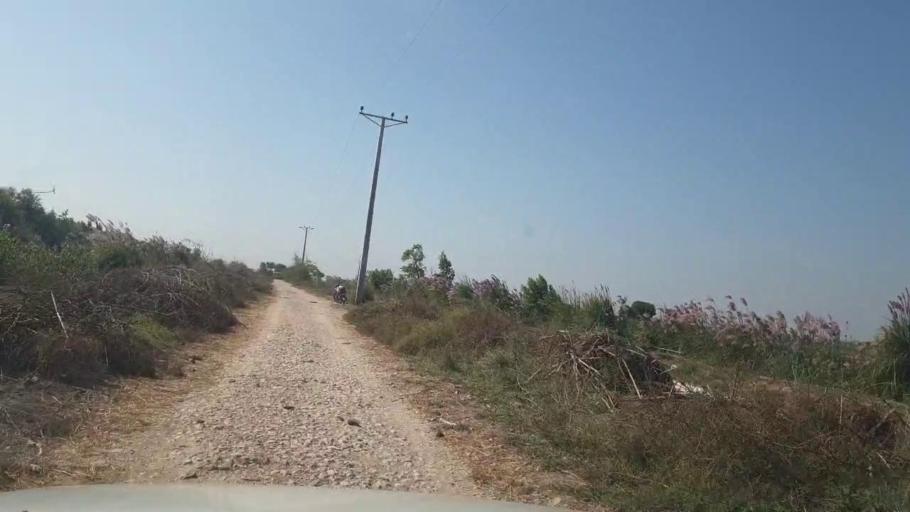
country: PK
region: Sindh
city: Chuhar Jamali
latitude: 24.4214
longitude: 67.8155
